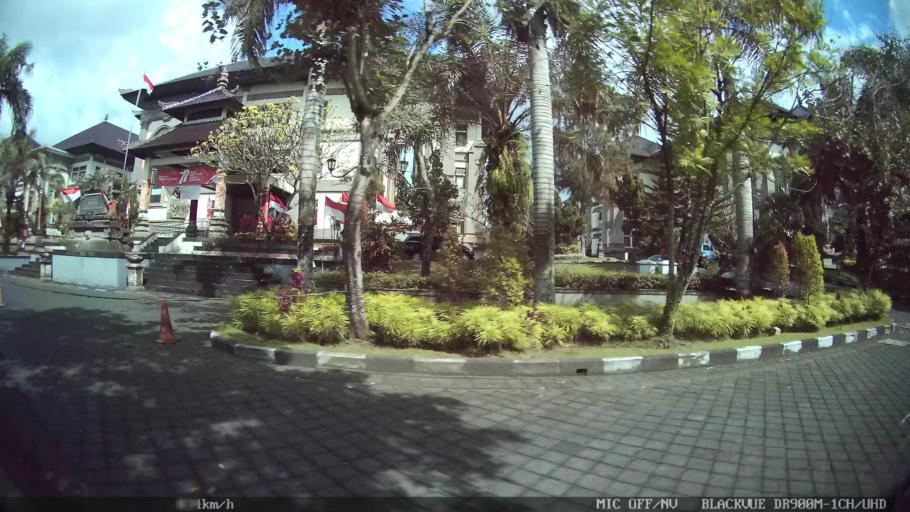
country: ID
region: Bali
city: Banjar Karangsuling
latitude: -8.6031
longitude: 115.1801
